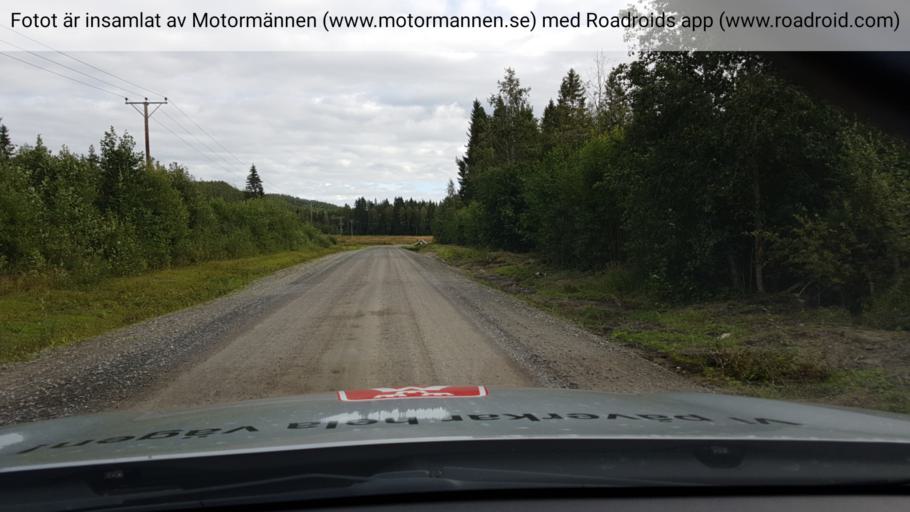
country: SE
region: Jaemtland
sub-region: Ragunda Kommun
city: Hammarstrand
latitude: 62.9372
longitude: 16.1269
